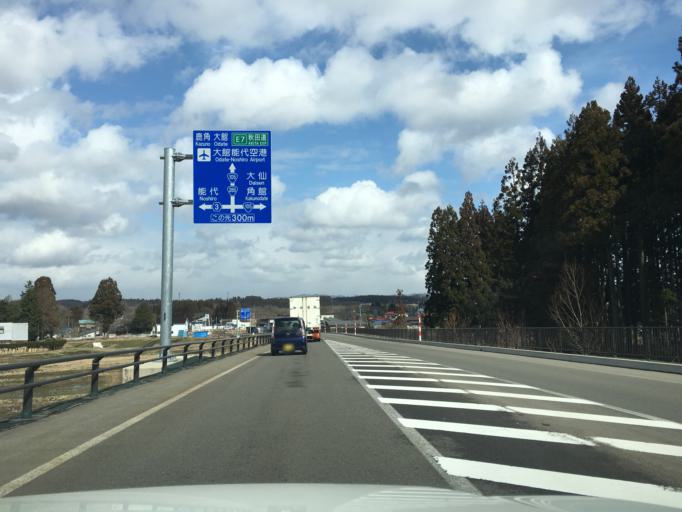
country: JP
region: Akita
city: Takanosu
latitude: 40.1169
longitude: 140.3772
